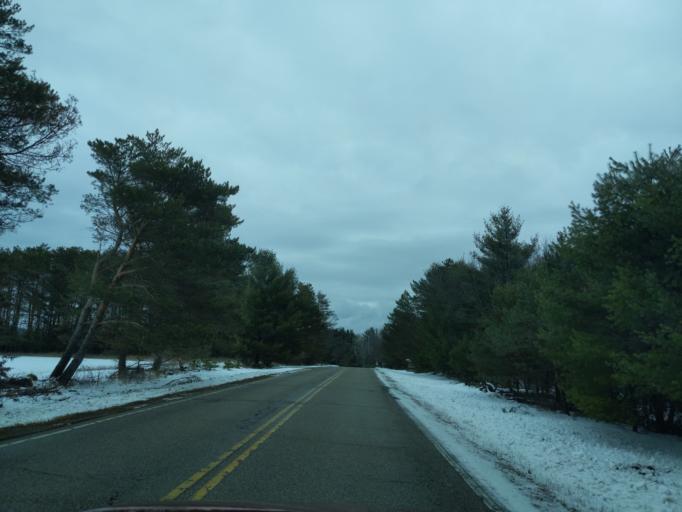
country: US
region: Wisconsin
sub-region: Marquette County
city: Montello
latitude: 43.9103
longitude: -89.3646
